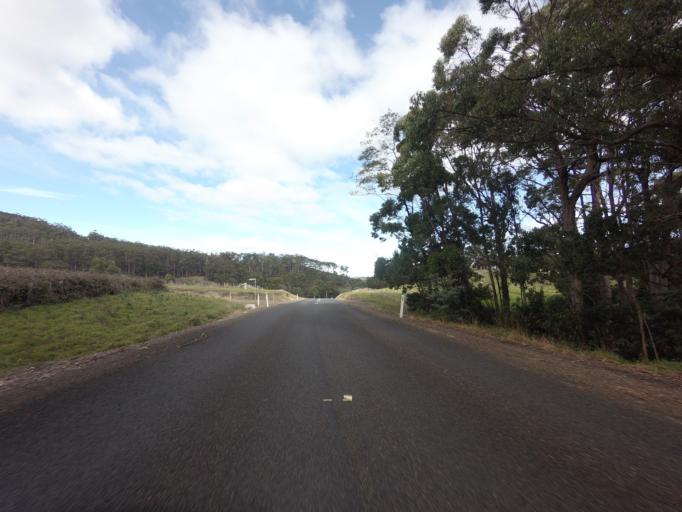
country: AU
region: Tasmania
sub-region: Clarence
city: Sandford
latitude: -43.0751
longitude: 147.7496
